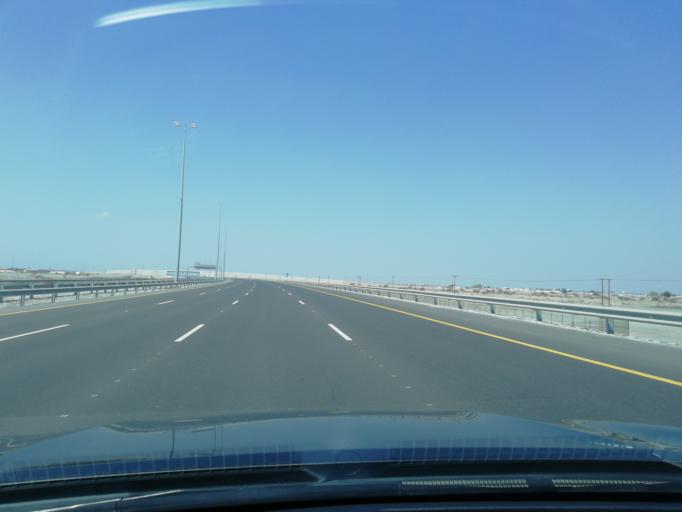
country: OM
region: Al Batinah
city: Barka'
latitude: 23.6299
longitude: 57.8530
